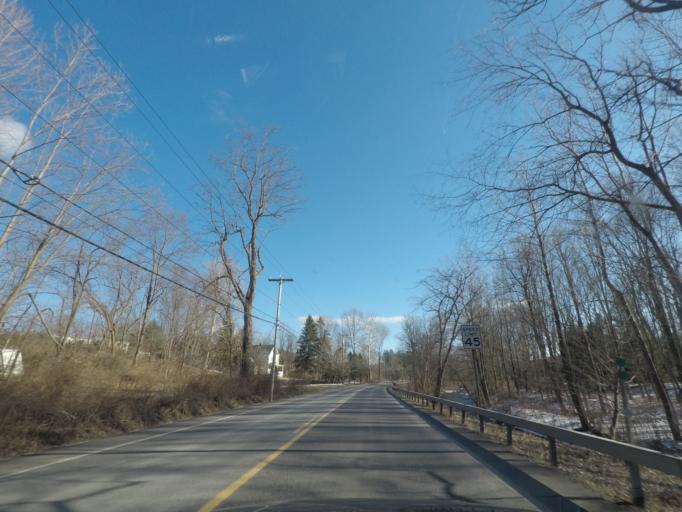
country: US
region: New York
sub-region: Columbia County
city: Chatham
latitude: 42.3376
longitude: -73.5581
